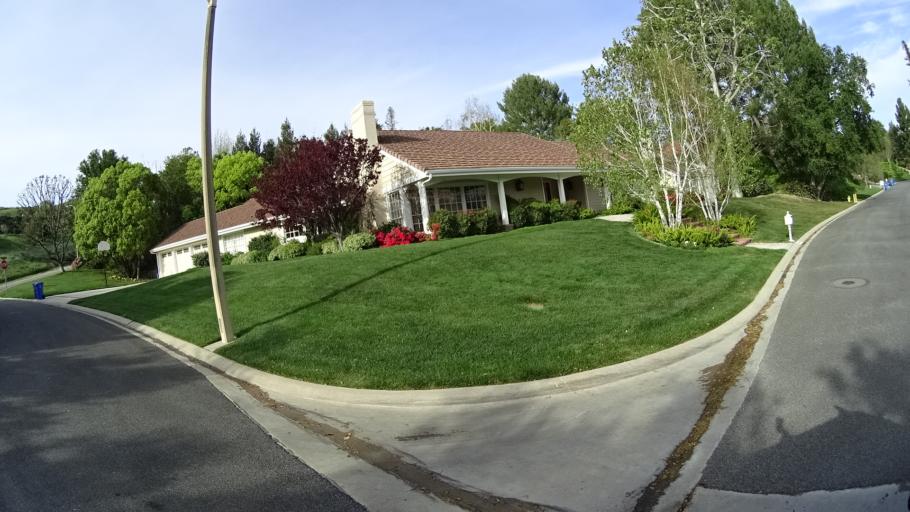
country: US
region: California
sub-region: Ventura County
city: Thousand Oaks
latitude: 34.1895
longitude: -118.8043
